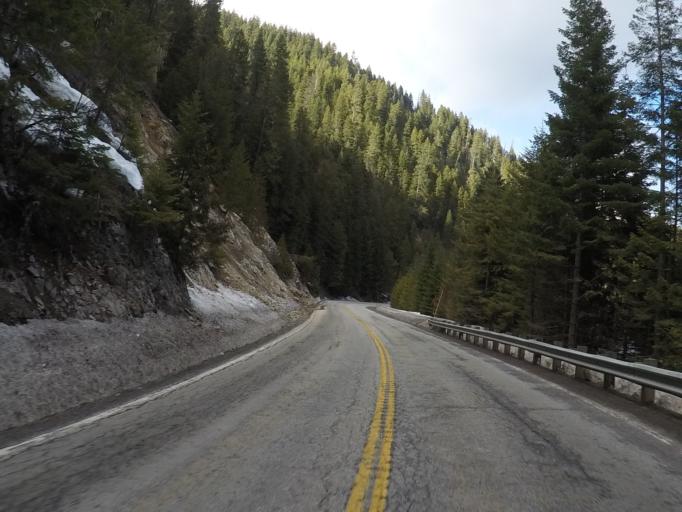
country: US
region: Montana
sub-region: Mineral County
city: Superior
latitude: 46.4900
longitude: -114.8702
